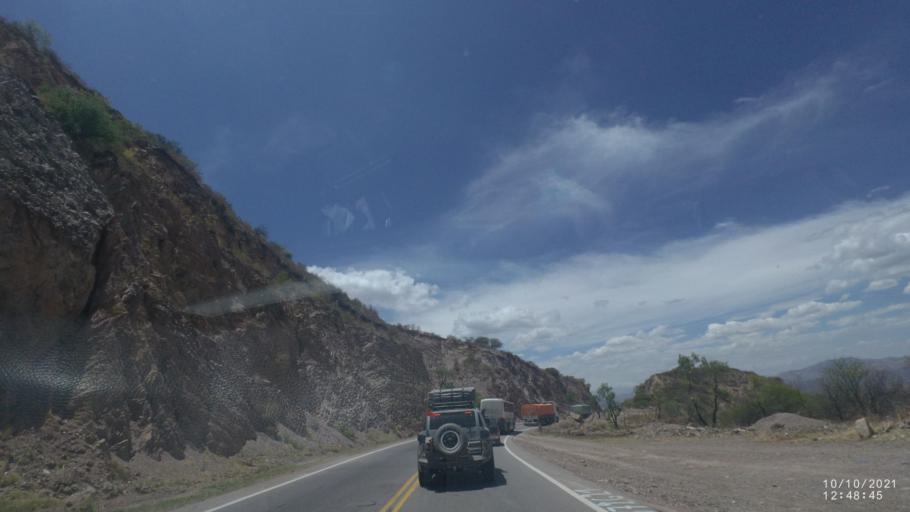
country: BO
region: Cochabamba
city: Irpa Irpa
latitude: -17.6244
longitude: -66.3591
